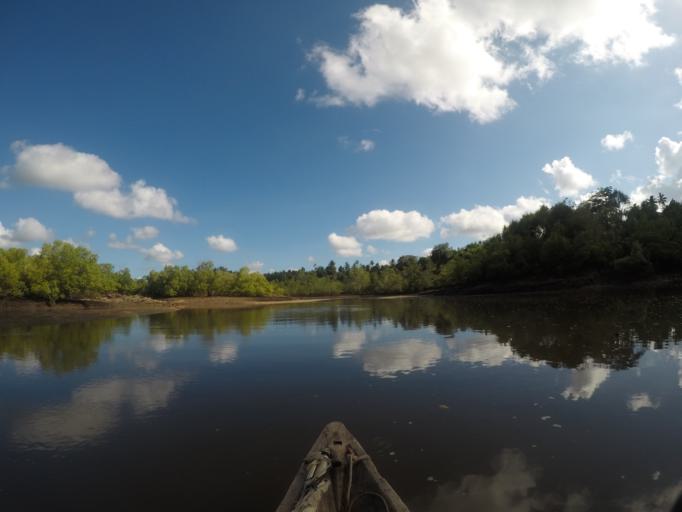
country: TZ
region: Pemba South
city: Mtambile
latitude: -5.3433
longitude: 39.6911
